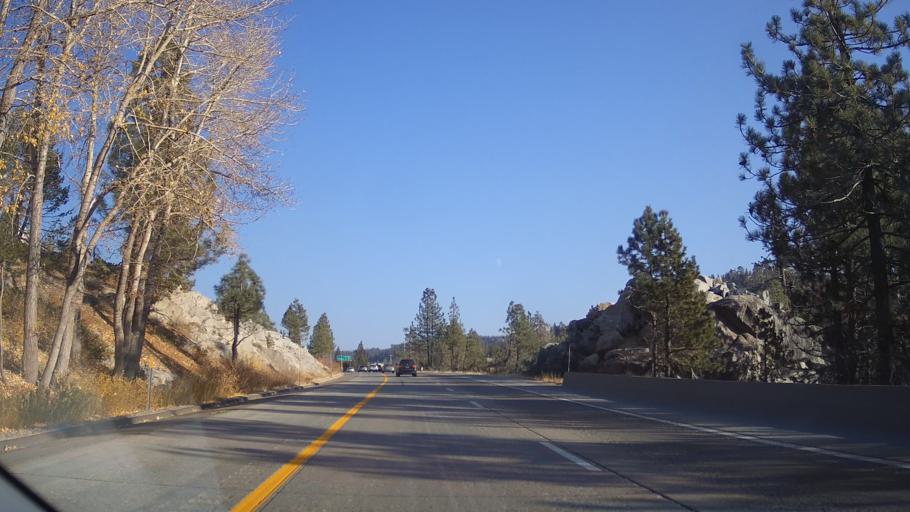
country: US
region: California
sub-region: Nevada County
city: Truckee
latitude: 39.3124
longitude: -120.5076
